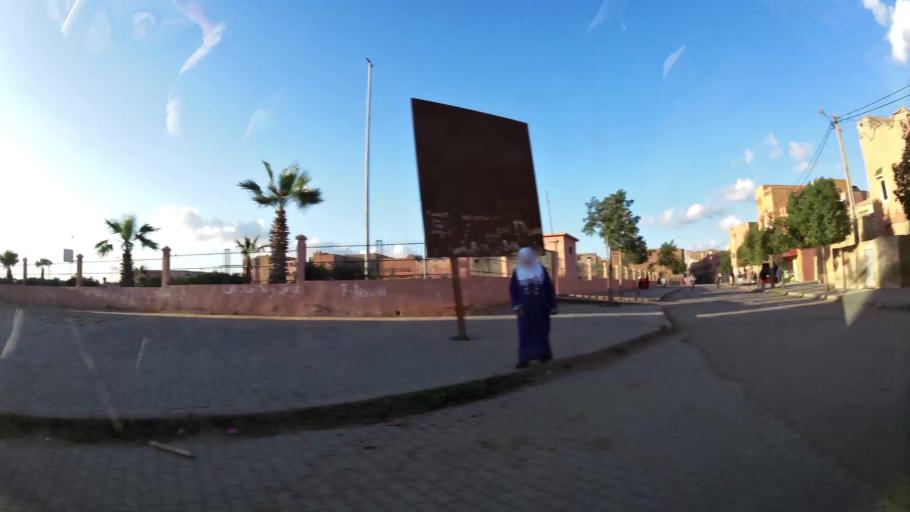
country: MA
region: Marrakech-Tensift-Al Haouz
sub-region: Kelaa-Des-Sraghna
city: Sidi Abdallah
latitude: 32.2472
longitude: -7.9468
